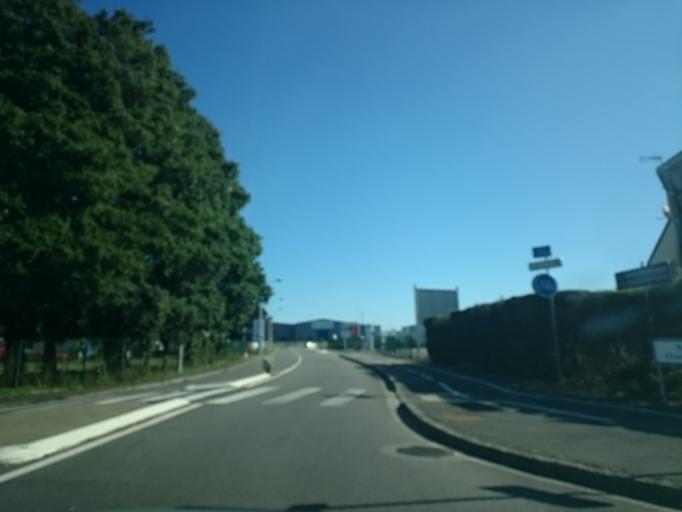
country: FR
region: Brittany
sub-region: Departement du Finistere
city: Gouesnou
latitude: 48.4243
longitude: -4.4603
